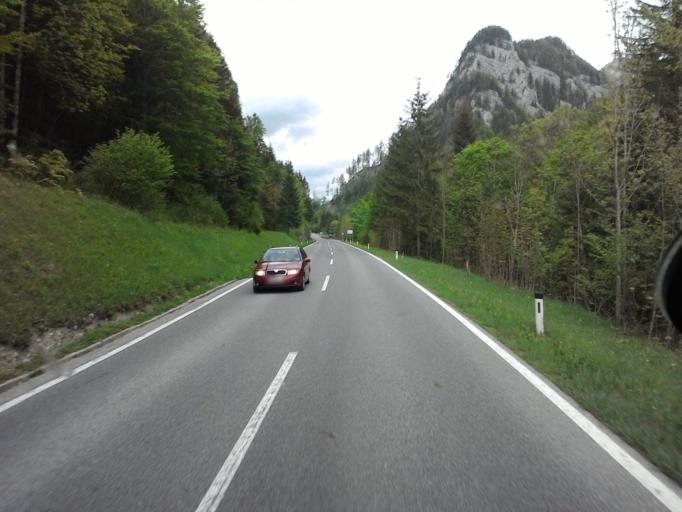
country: AT
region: Styria
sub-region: Politischer Bezirk Liezen
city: Palfau
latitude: 47.7107
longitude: 14.8265
